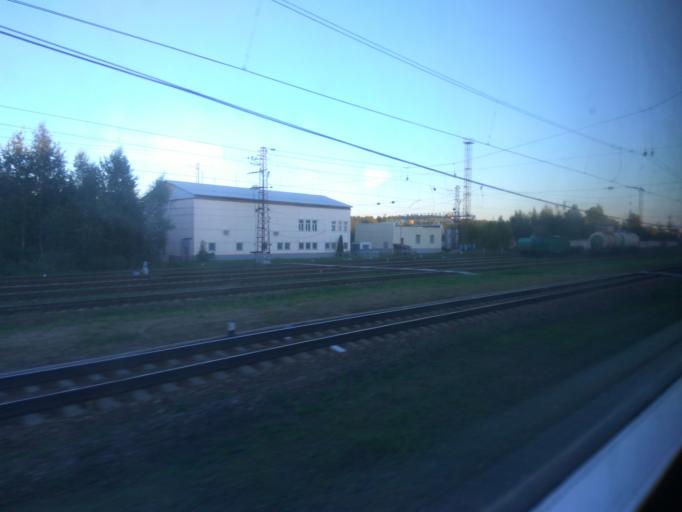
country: RU
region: Moskovskaya
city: Elektrostal'
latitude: 55.7712
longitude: 38.4677
